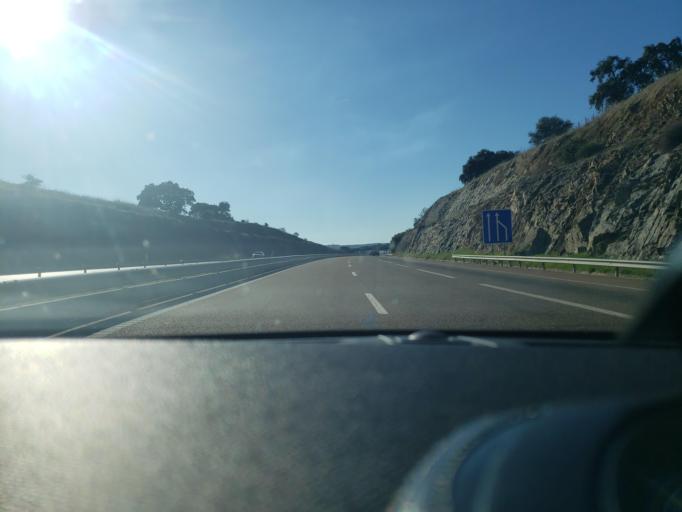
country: PT
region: Portalegre
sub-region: Elvas
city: Elvas
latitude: 38.9057
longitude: -7.1873
